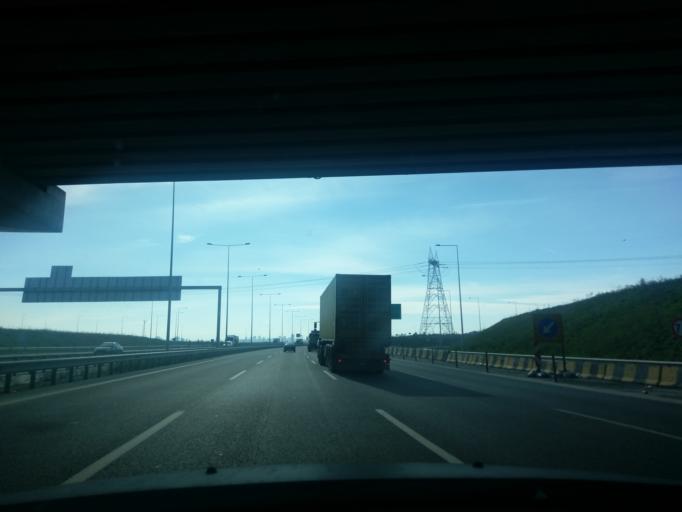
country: TR
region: Istanbul
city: Basaksehir
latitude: 41.1163
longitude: 28.8153
